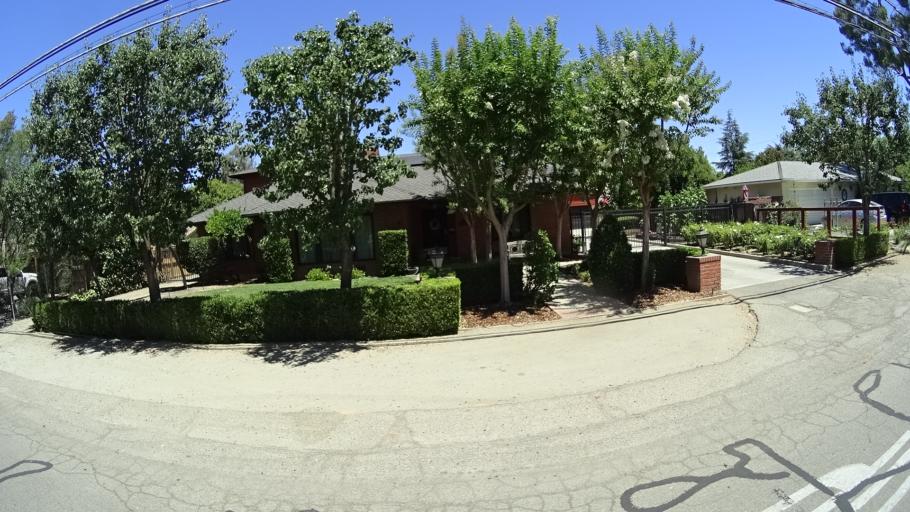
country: US
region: California
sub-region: Fresno County
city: Fresno
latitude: 36.7876
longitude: -119.8030
